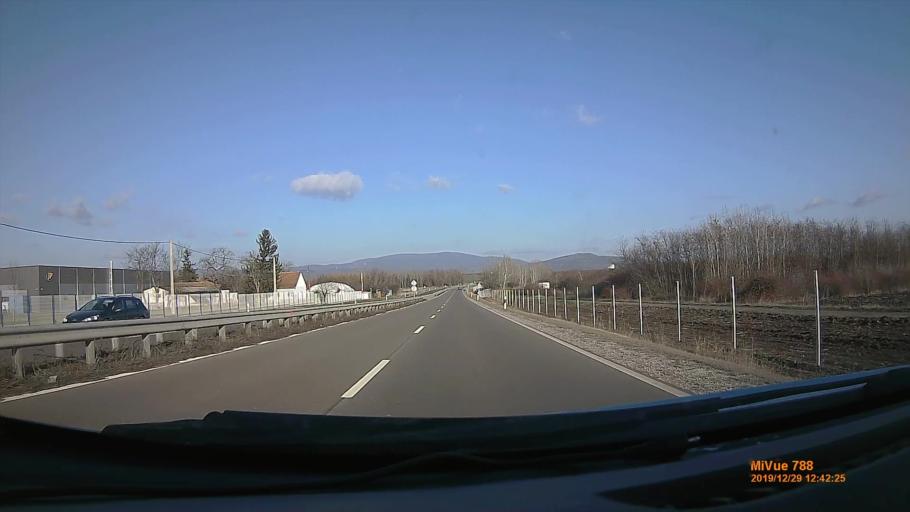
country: HU
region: Heves
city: Nagyrede
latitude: 47.7432
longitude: 19.8734
